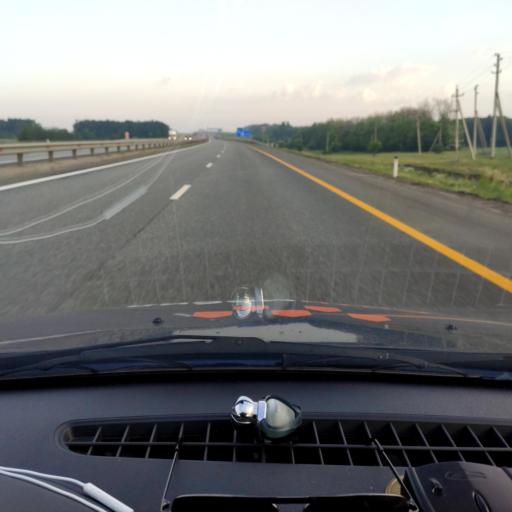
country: RU
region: Lipetsk
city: Zadonsk
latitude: 52.5356
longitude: 38.7350
